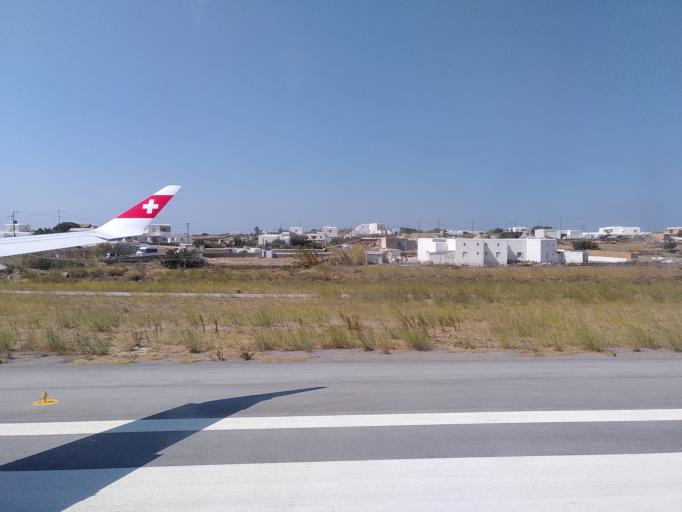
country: GR
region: South Aegean
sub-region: Nomos Kykladon
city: Mykonos
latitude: 37.4310
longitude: 25.3501
